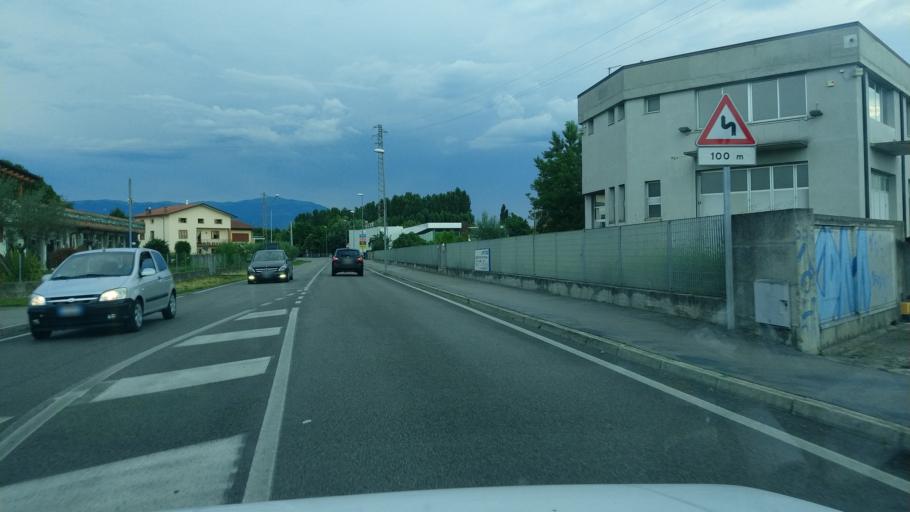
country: IT
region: Veneto
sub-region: Provincia di Vicenza
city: Nove
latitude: 45.7114
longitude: 11.6766
